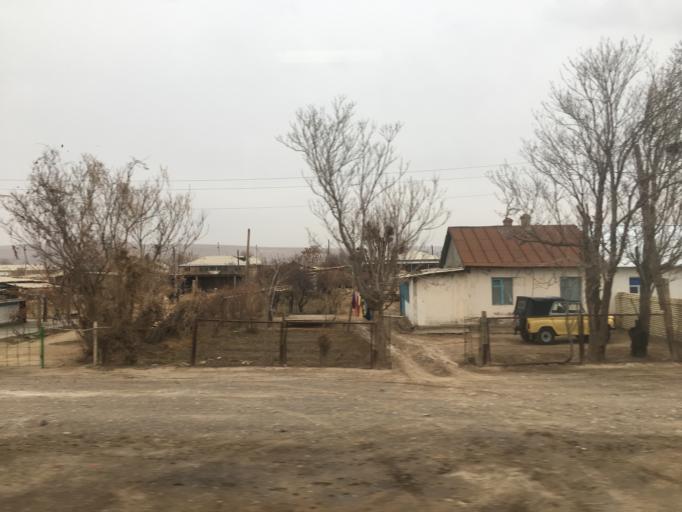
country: TM
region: Mary
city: Yoloeten
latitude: 36.5358
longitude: 62.5540
